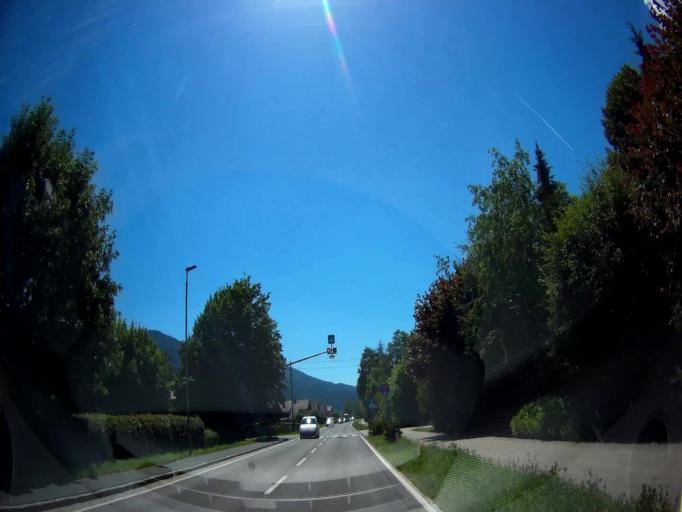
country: AT
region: Carinthia
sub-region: Politischer Bezirk Sankt Veit an der Glan
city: Gurk
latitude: 46.8741
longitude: 14.2867
